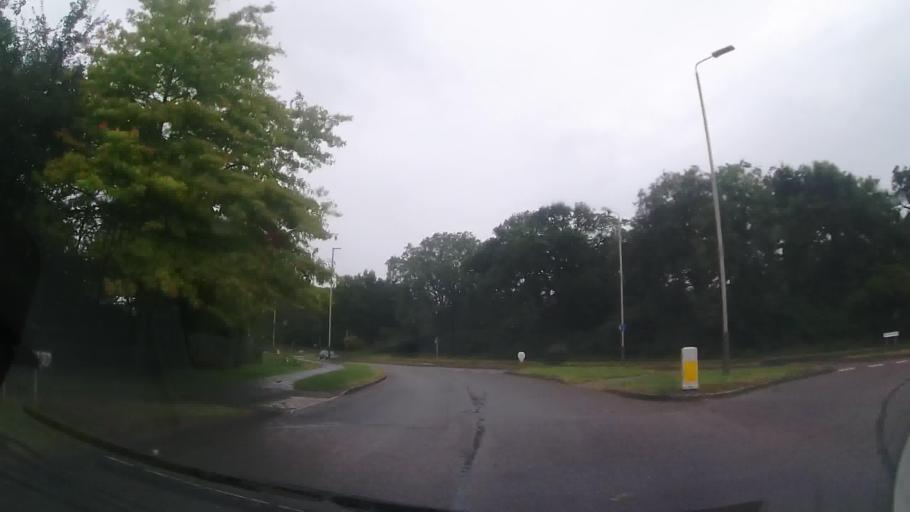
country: GB
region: England
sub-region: Leicestershire
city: Anstey
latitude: 52.6751
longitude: -1.1530
